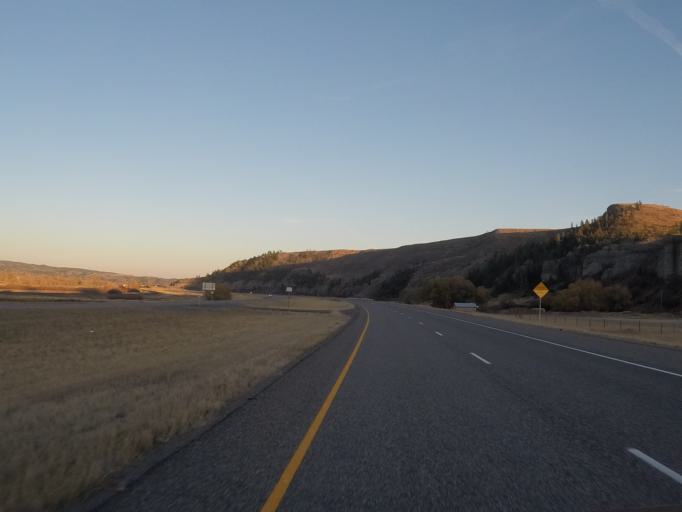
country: US
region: Montana
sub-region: Sweet Grass County
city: Big Timber
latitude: 45.7326
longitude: -109.7504
